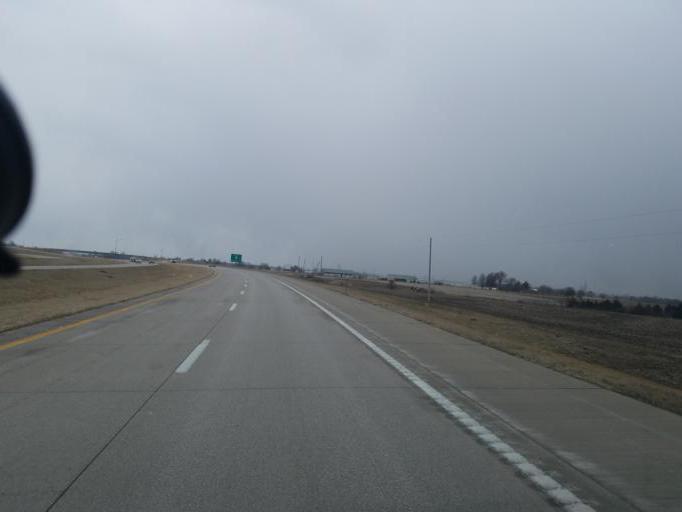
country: US
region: Missouri
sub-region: Randolph County
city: Moberly
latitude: 39.4611
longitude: -92.4352
